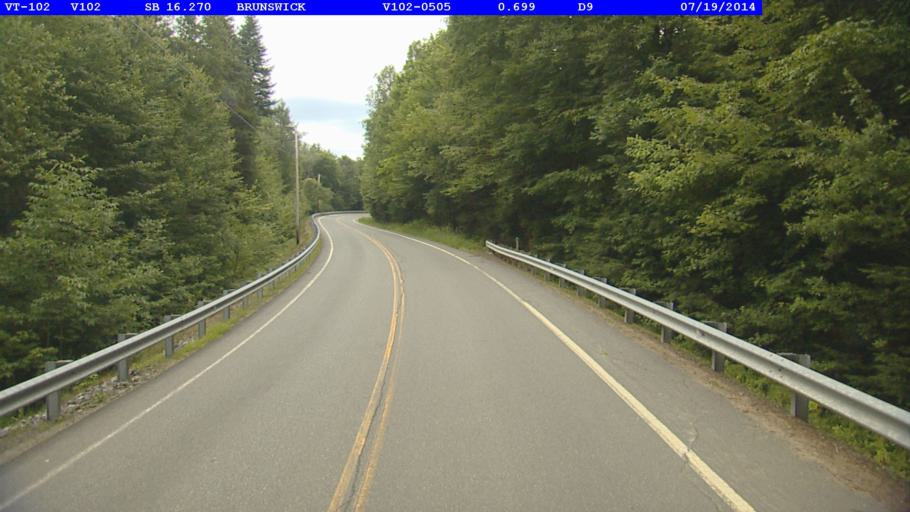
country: US
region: New Hampshire
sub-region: Coos County
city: Stratford
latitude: 44.6715
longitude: -71.5945
